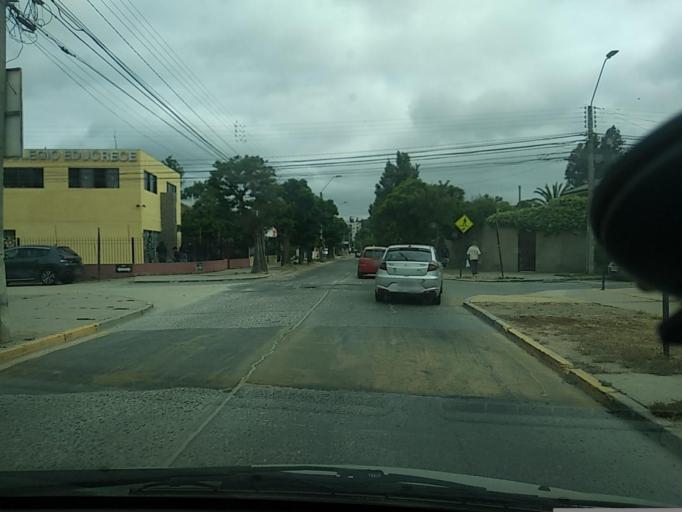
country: CL
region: Valparaiso
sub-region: Provincia de Marga Marga
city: Villa Alemana
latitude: -33.0413
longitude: -71.3761
